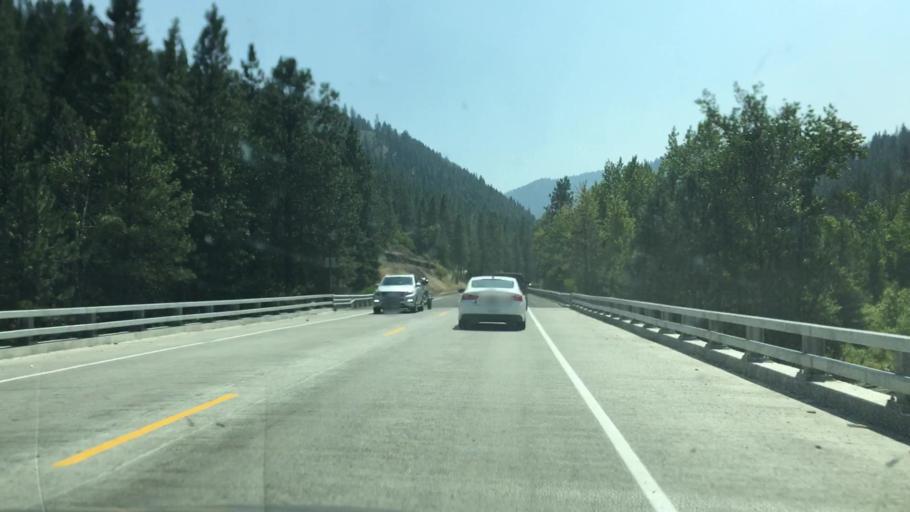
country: US
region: Idaho
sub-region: Valley County
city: McCall
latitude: 45.1808
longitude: -116.3016
